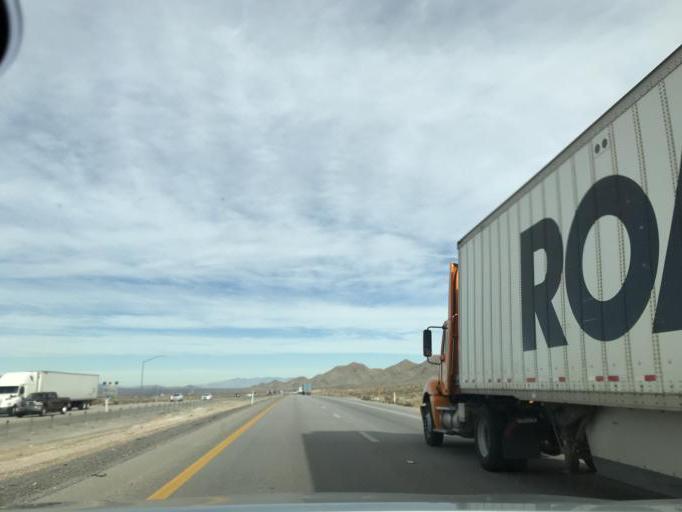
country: US
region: Nevada
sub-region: Clark County
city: Nellis Air Force Base
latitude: 36.3375
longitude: -114.9176
